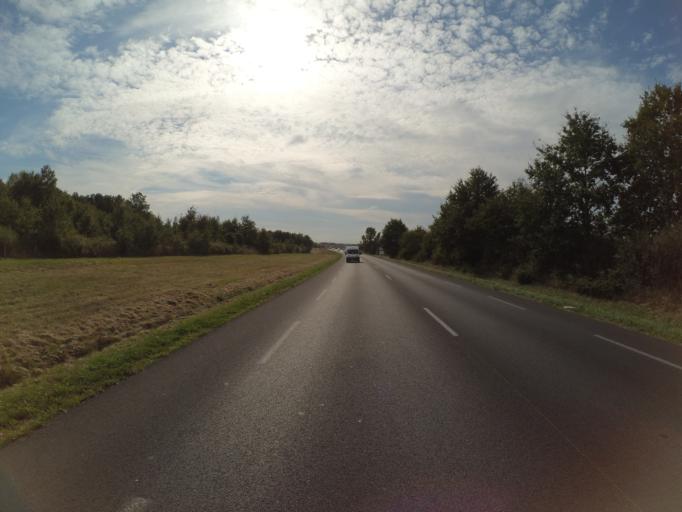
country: FR
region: Pays de la Loire
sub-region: Departement de Maine-et-Loire
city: Distre
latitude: 47.2393
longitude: -0.1117
